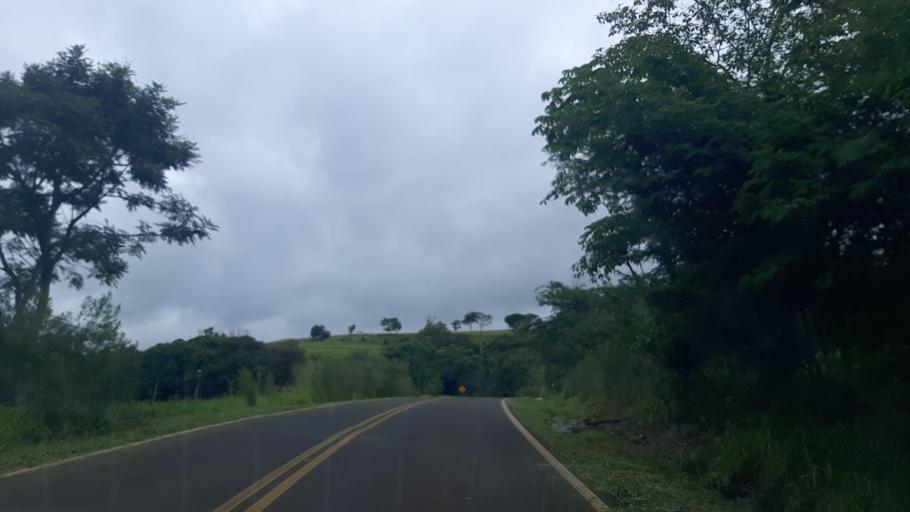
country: BR
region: Parana
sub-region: Ampere
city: Ampere
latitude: -25.9421
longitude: -53.4624
